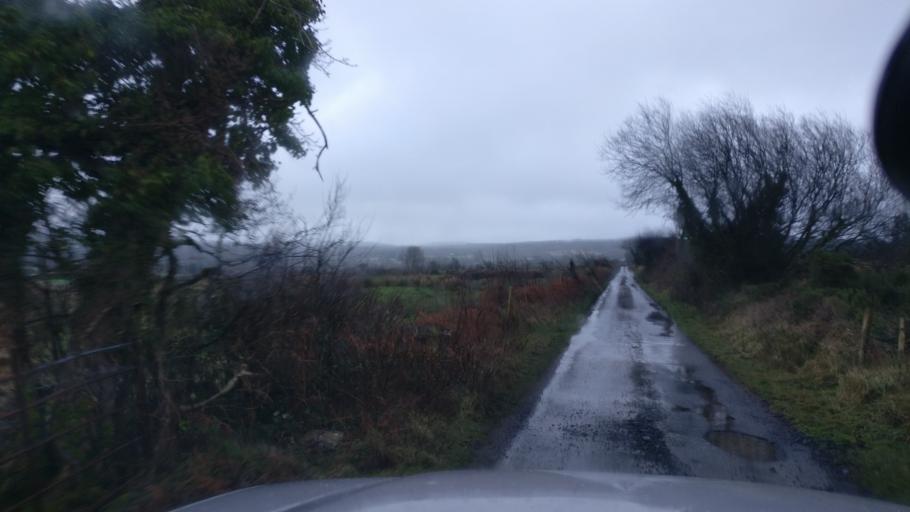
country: IE
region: Connaught
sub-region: County Galway
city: Loughrea
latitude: 53.1525
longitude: -8.6334
